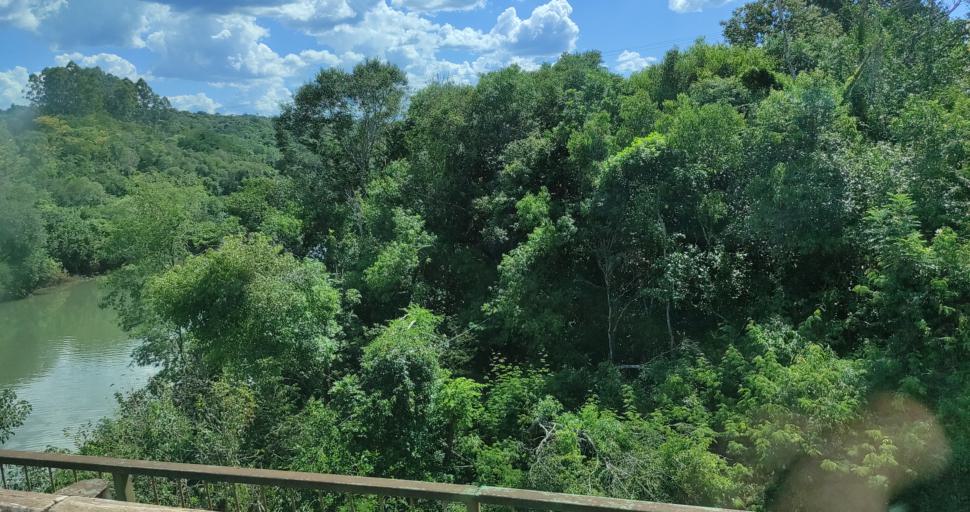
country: AR
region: Misiones
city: El Soberbio
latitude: -27.2798
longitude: -54.1968
